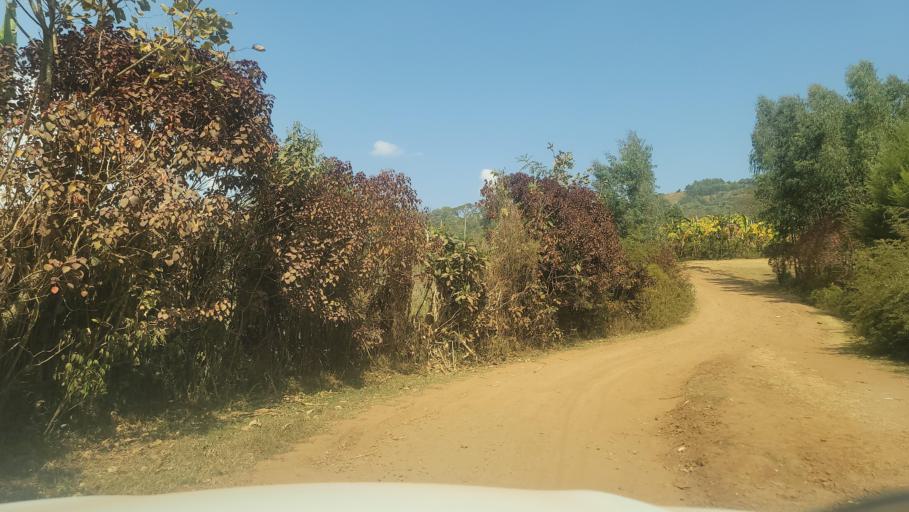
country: ET
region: Oromiya
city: Agaro
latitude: 7.8385
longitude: 36.5352
